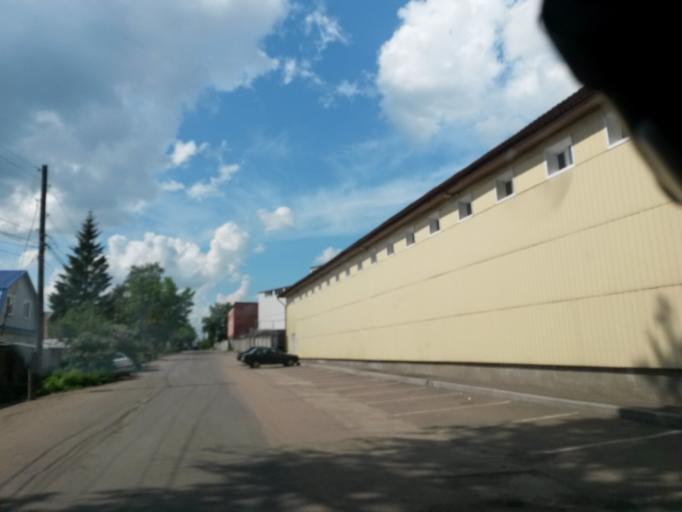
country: RU
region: Jaroslavl
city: Yaroslavl
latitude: 57.6021
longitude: 39.8923
